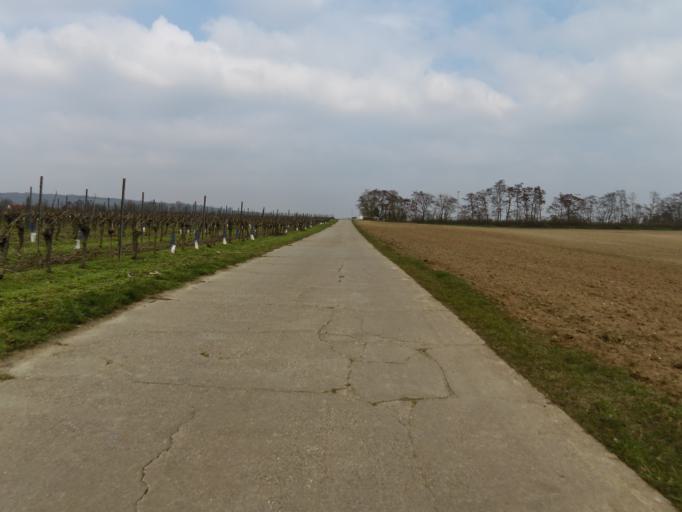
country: DE
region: Rheinland-Pfalz
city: Heidesheim
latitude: 49.5776
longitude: 8.1836
